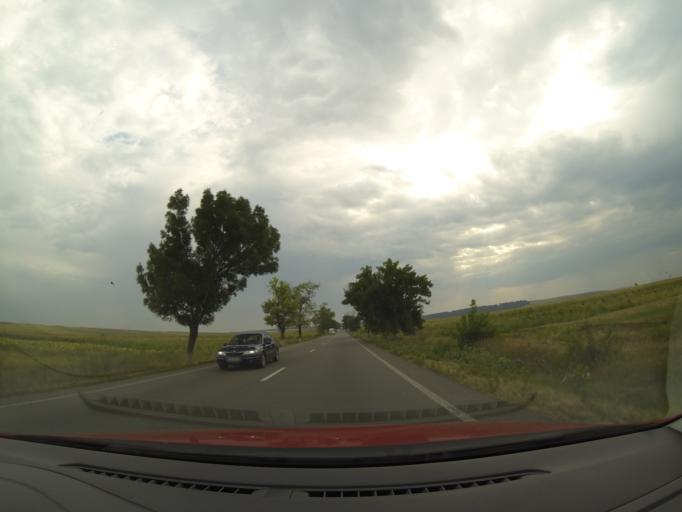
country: RO
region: Olt
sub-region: Comuna Bobicesti
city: Bobicesti
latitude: 44.3570
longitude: 24.1675
